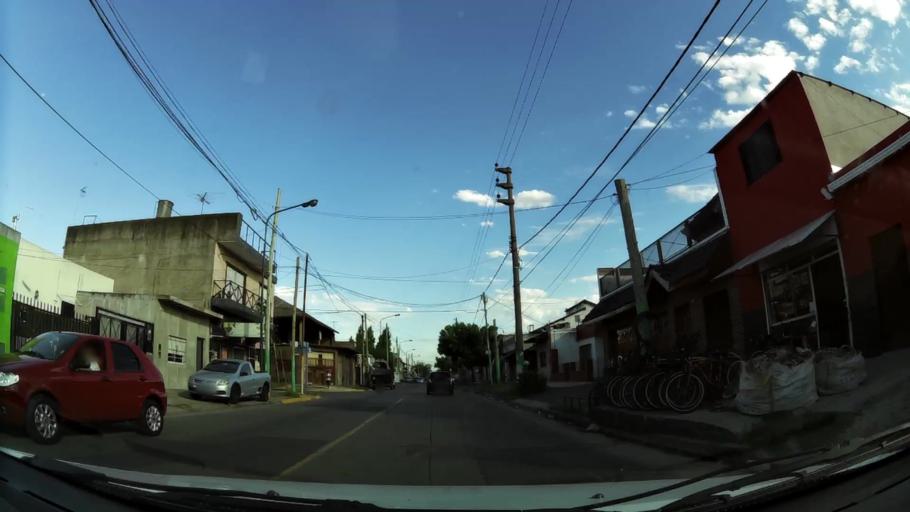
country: AR
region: Buenos Aires
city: Hurlingham
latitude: -34.5767
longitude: -58.6077
